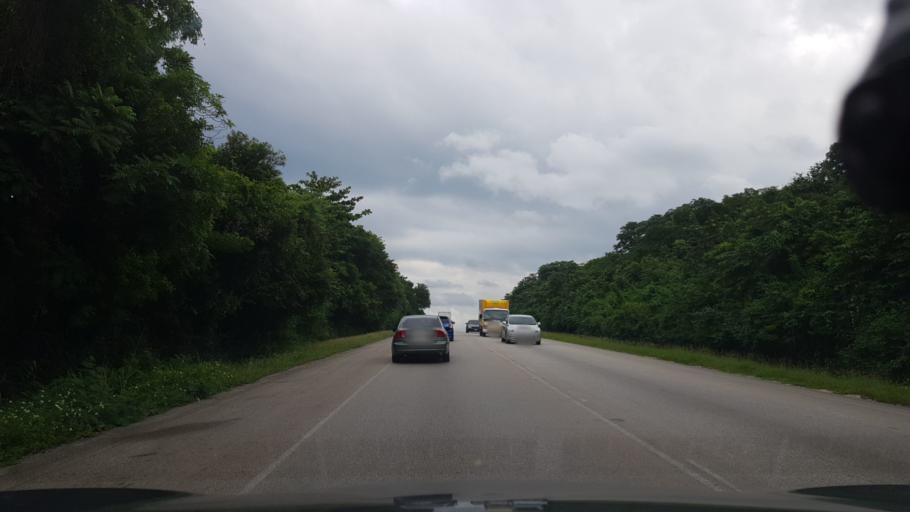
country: JM
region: Saint Ann
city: Runaway Bay
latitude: 18.4622
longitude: -77.2801
